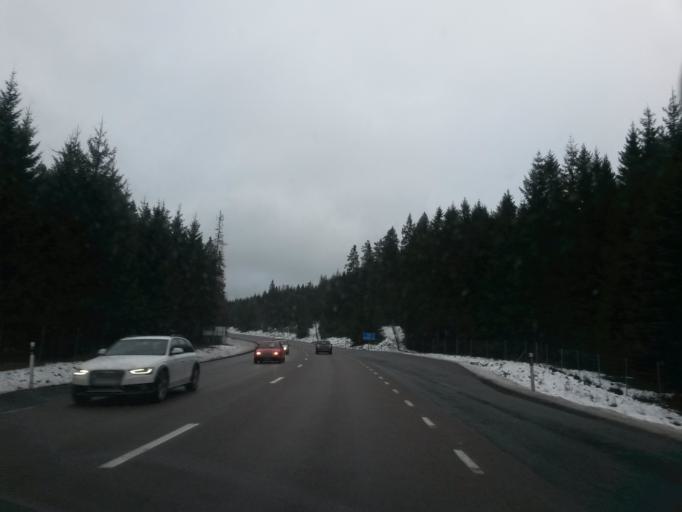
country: SE
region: Vaestra Goetaland
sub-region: Boras Kommun
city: Viskafors
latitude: 57.6157
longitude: 12.8795
